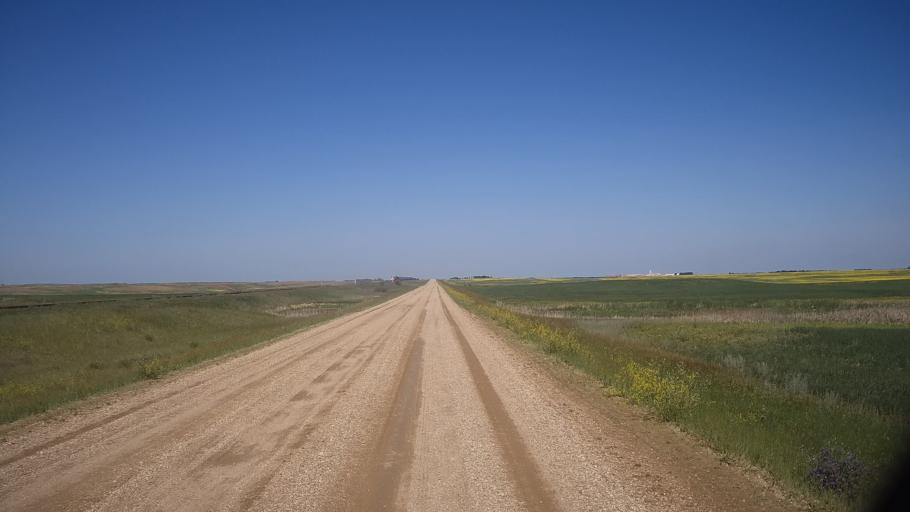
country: CA
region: Saskatchewan
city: Watrous
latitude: 51.8536
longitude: -105.9434
